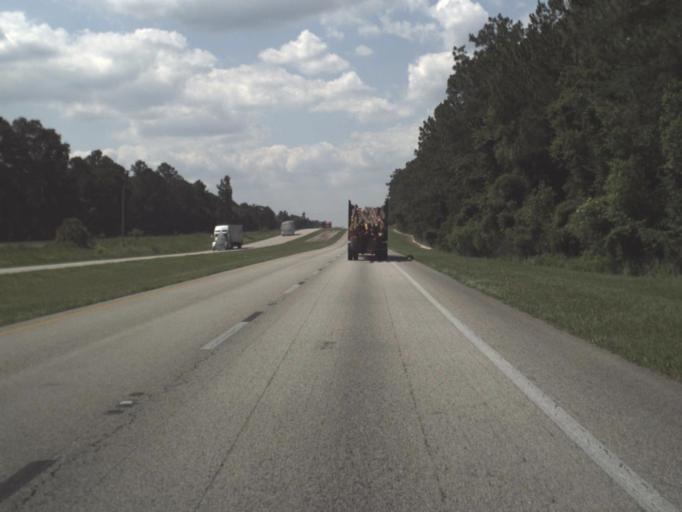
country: US
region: Florida
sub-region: Alachua County
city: Hawthorne
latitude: 29.6884
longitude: -82.1273
